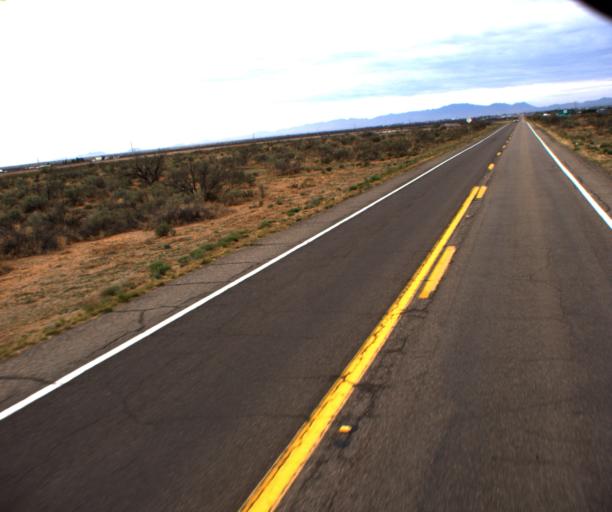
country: US
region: Arizona
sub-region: Cochise County
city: Willcox
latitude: 32.3012
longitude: -109.7987
